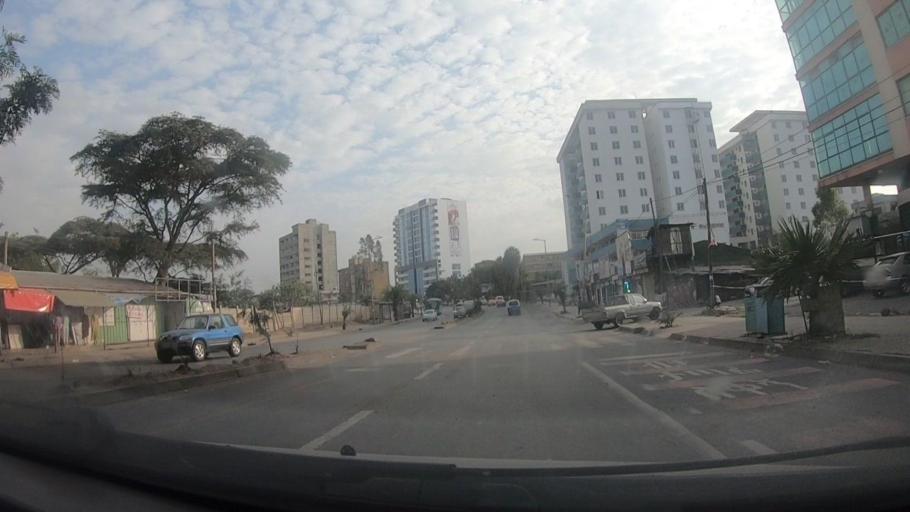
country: ET
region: Adis Abeba
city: Addis Ababa
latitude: 8.9693
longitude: 38.7313
